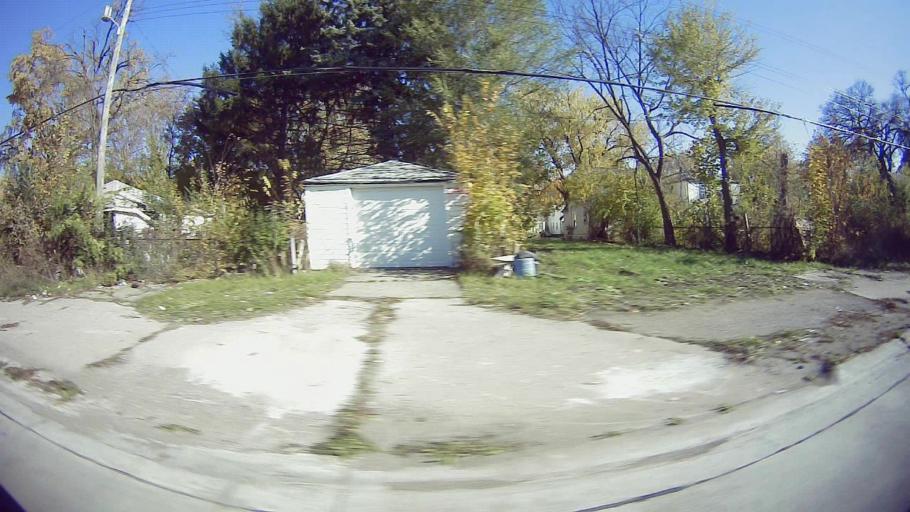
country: US
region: Michigan
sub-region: Wayne County
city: Redford
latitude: 42.4280
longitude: -83.2773
